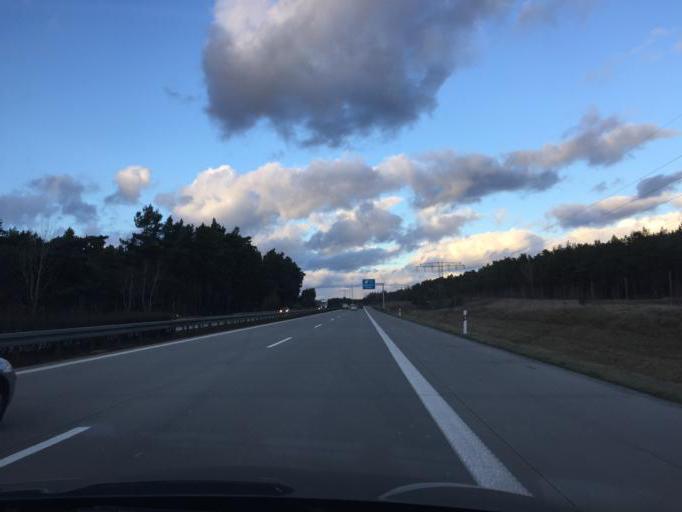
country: DE
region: Brandenburg
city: Schwerin
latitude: 52.1437
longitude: 13.6490
